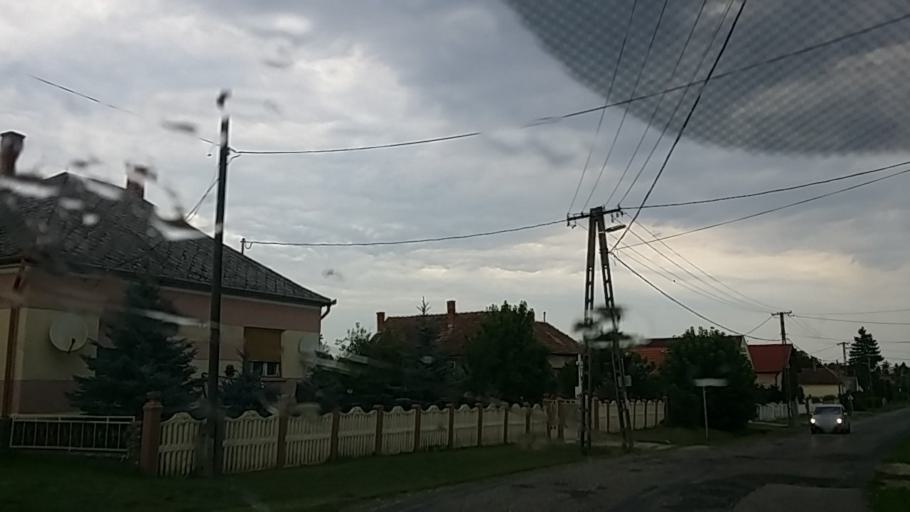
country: HU
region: Zala
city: Zalakomar
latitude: 46.5219
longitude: 17.1263
